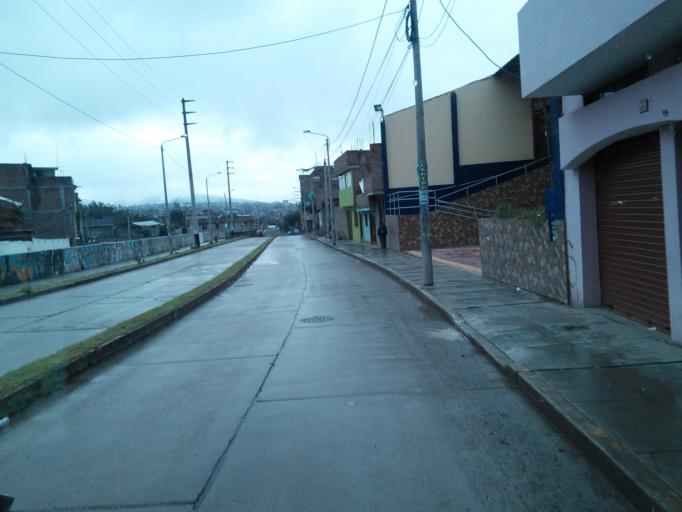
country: PE
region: Ayacucho
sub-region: Provincia de Huamanga
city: Ayacucho
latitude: -13.1681
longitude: -74.2262
